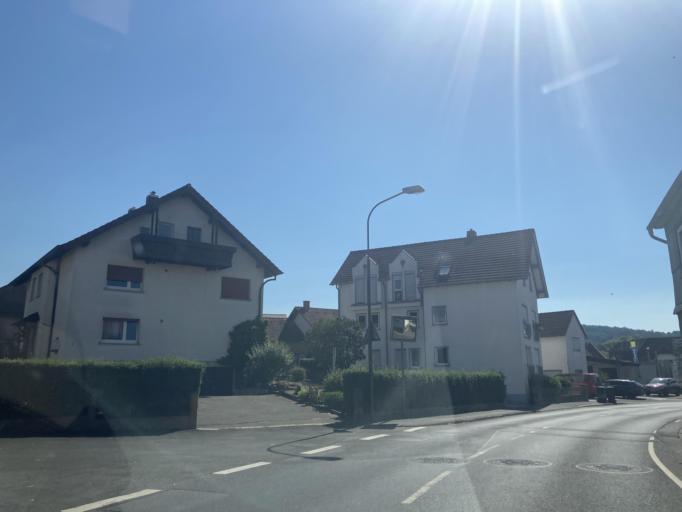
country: DE
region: Hesse
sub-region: Regierungsbezirk Kassel
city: Neuhof
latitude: 50.4565
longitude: 9.6129
